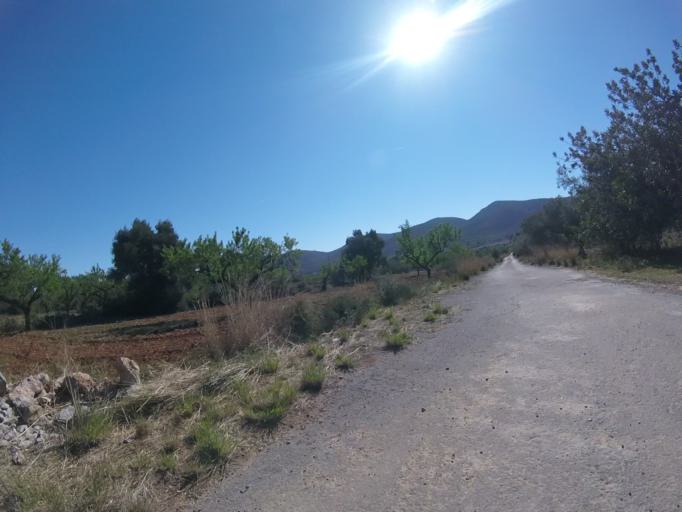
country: ES
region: Valencia
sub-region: Provincia de Castello
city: Santa Magdalena de Pulpis
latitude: 40.3560
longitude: 0.2843
